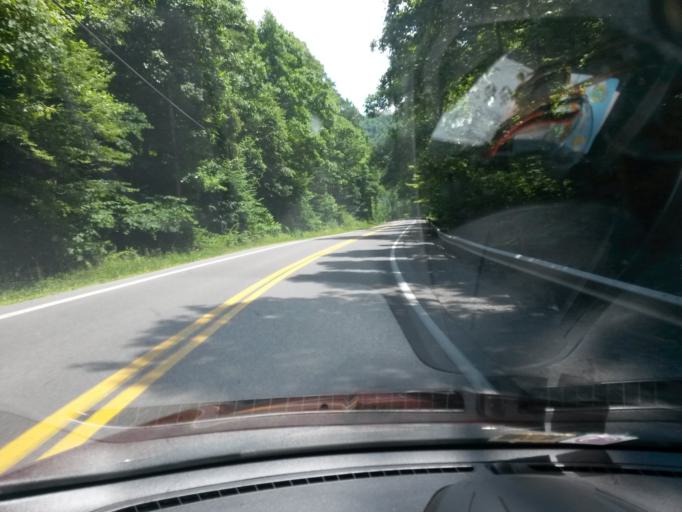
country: US
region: West Virginia
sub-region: Wyoming County
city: Pineville
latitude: 37.5630
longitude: -81.5350
